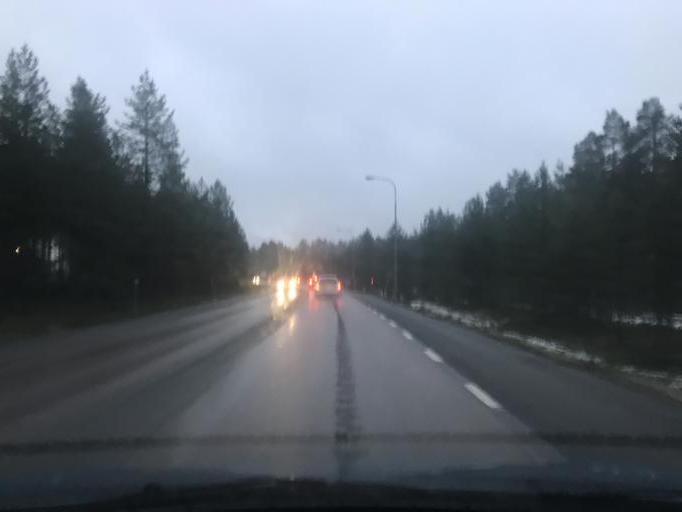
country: SE
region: Norrbotten
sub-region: Lulea Kommun
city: Gammelstad
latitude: 65.6221
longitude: 22.0353
